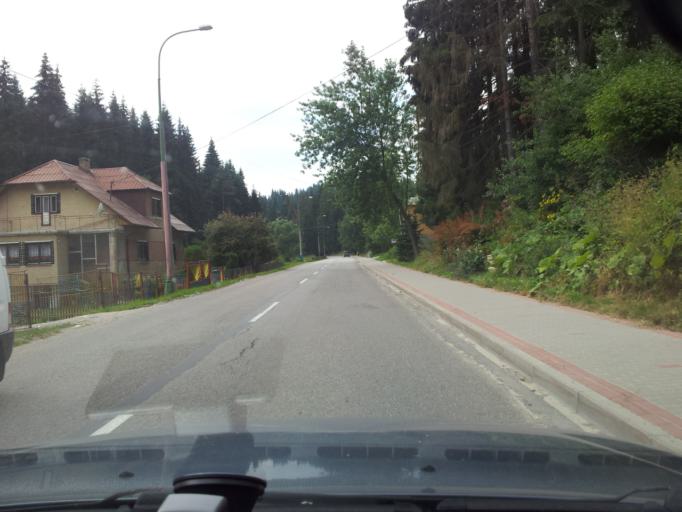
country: SK
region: Zilinsky
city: Oravska Lesna
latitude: 49.3709
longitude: 19.1912
